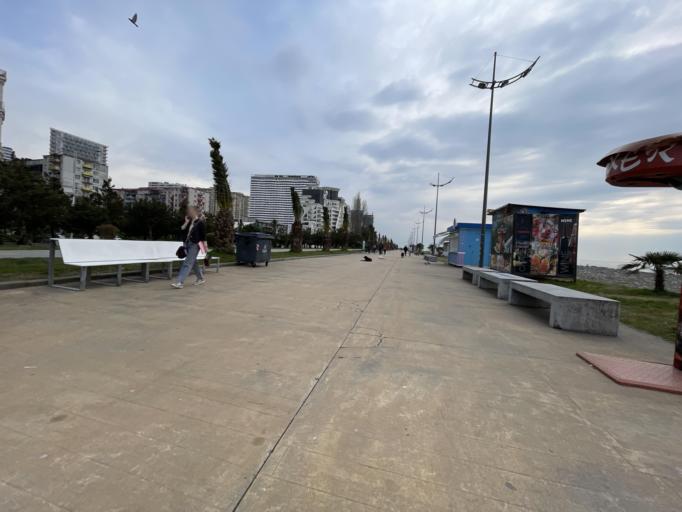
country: GE
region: Ajaria
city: Batumi
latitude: 41.6381
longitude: 41.6085
